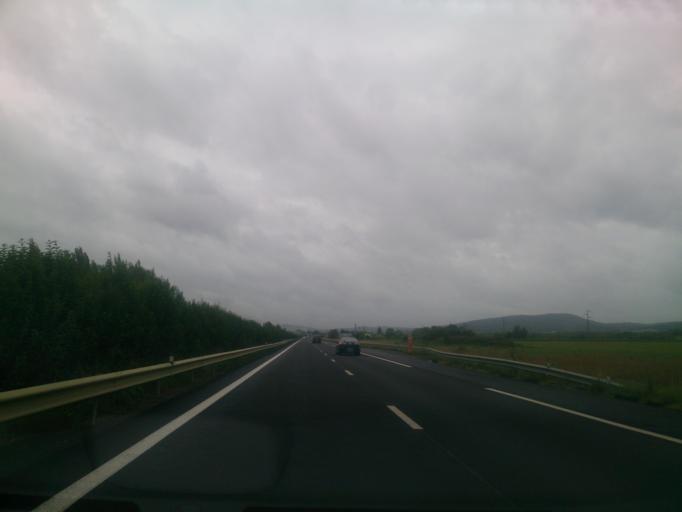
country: FR
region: Midi-Pyrenees
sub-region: Departement de la Haute-Garonne
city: Martres-Tolosane
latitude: 43.2185
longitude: 1.0435
